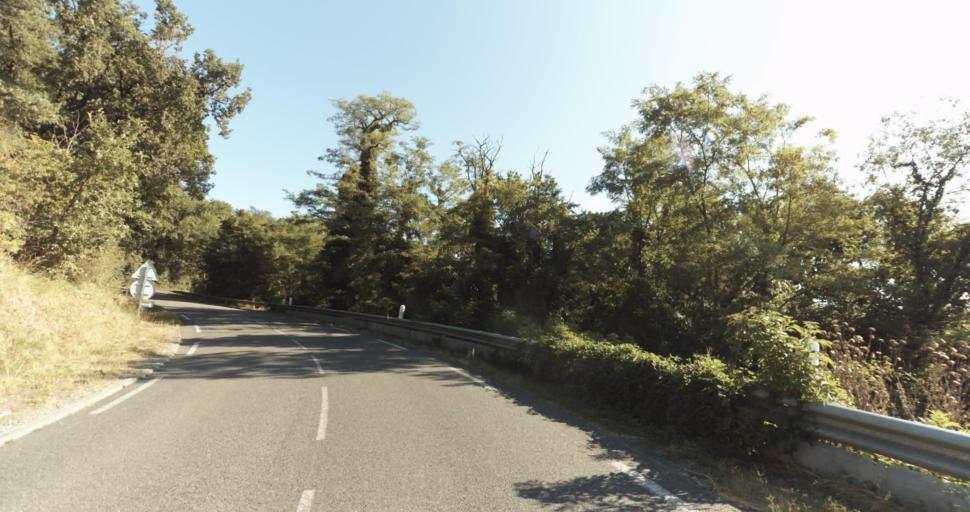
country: FR
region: Midi-Pyrenees
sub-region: Departement de la Haute-Garonne
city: L'Union
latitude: 43.6731
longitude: 1.4777
